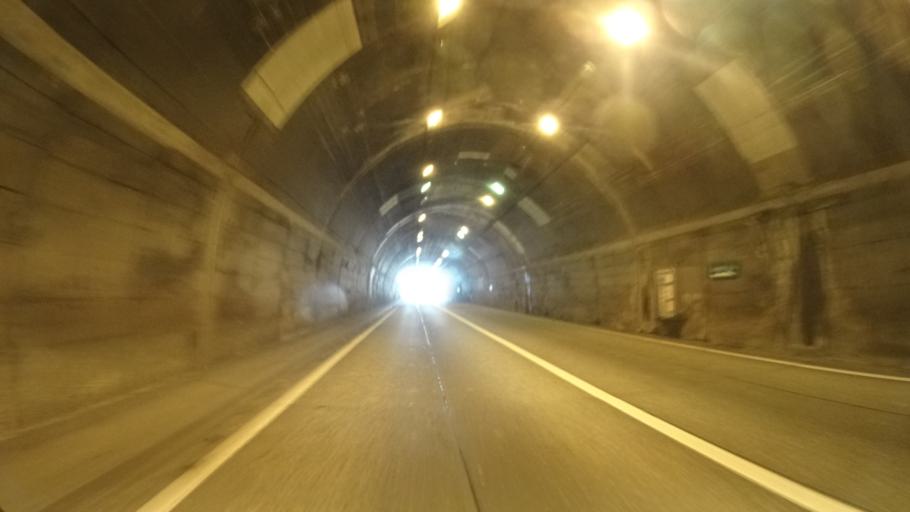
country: JP
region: Niigata
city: Kashiwazaki
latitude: 37.3221
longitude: 138.4448
